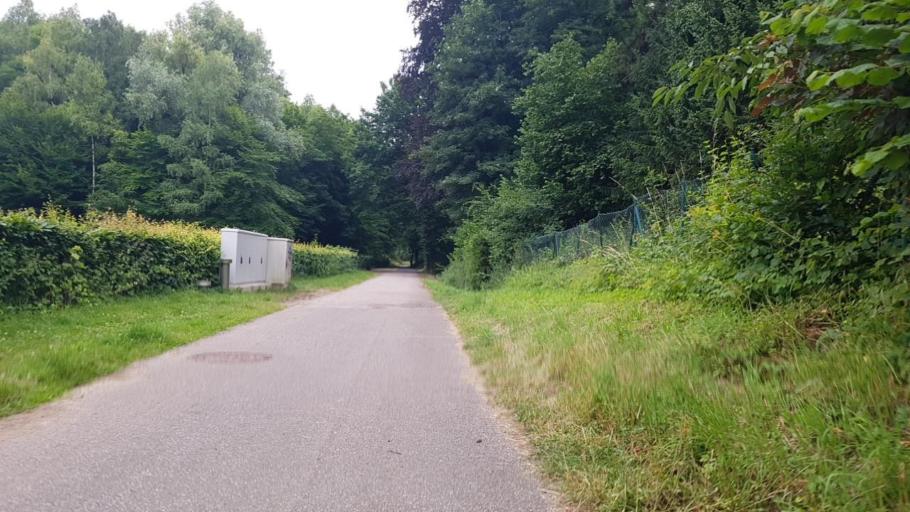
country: DE
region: North Rhine-Westphalia
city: Stolberg
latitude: 50.7475
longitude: 6.2605
